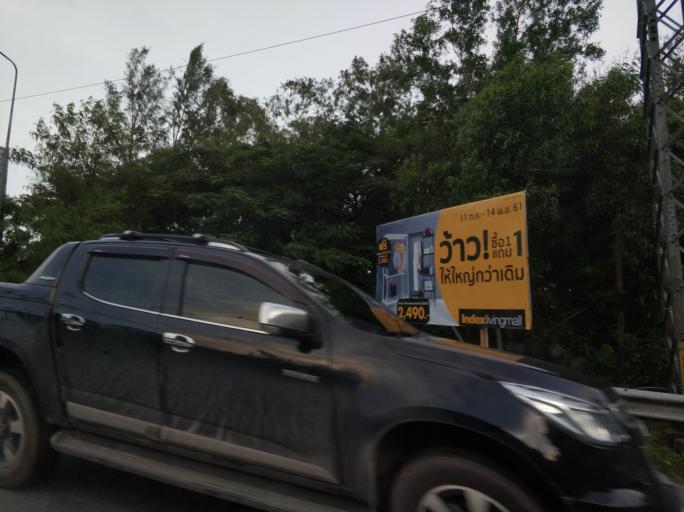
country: TH
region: Phuket
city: Kathu
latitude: 7.9050
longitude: 98.3243
